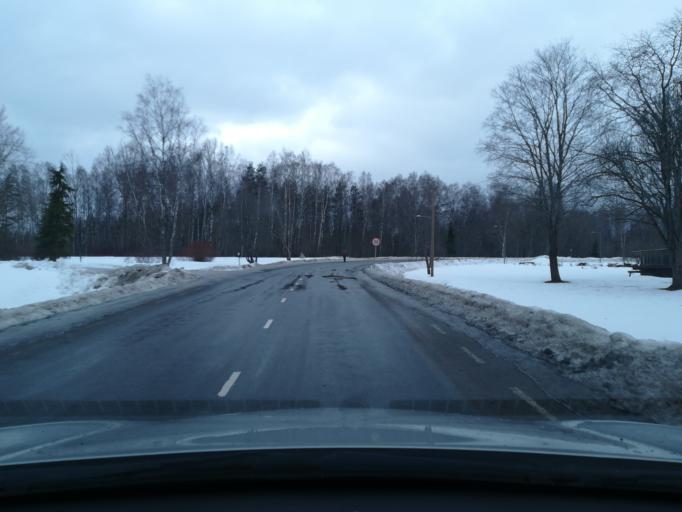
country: EE
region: Harju
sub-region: Nissi vald
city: Turba
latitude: 59.0739
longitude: 24.2437
